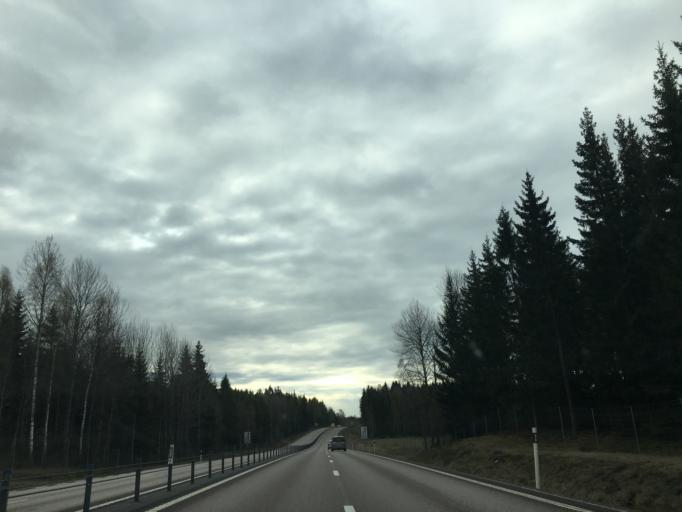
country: SE
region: Vaermland
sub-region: Kristinehamns Kommun
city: Kristinehamn
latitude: 59.3581
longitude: 14.0502
